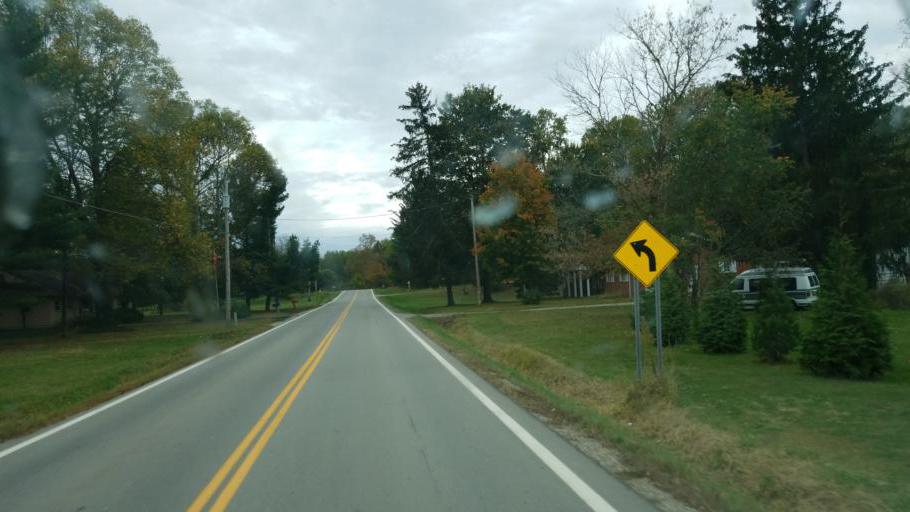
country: US
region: Ohio
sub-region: Huron County
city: Wakeman
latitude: 41.2006
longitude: -82.4059
